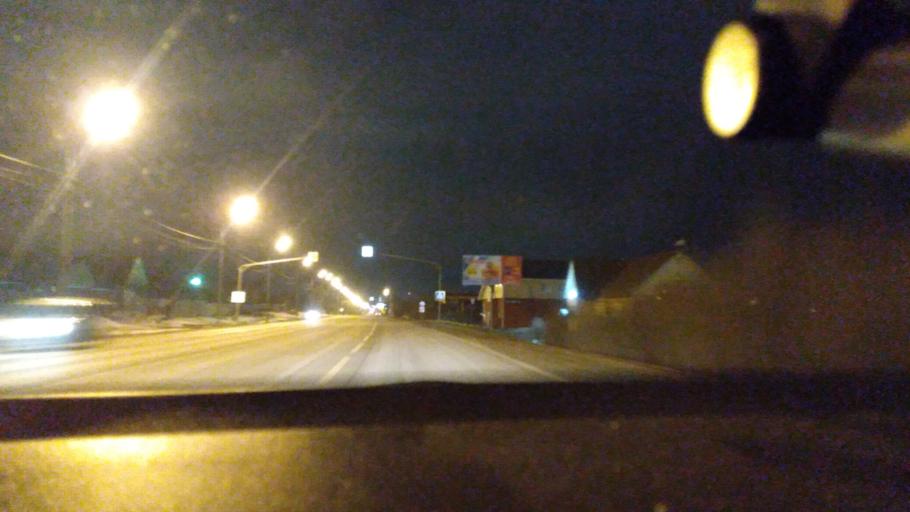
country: RU
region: Moskovskaya
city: Bronnitsy
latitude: 55.4072
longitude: 38.2984
